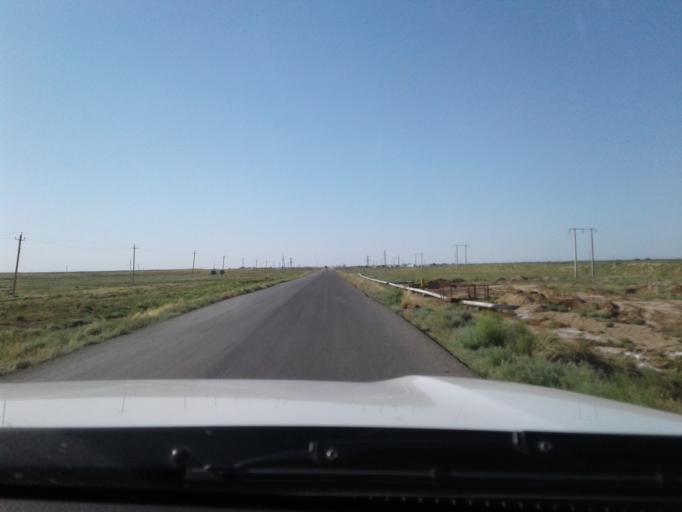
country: IR
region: Razavi Khorasan
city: Kalat-e Naderi
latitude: 37.1784
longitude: 60.0432
